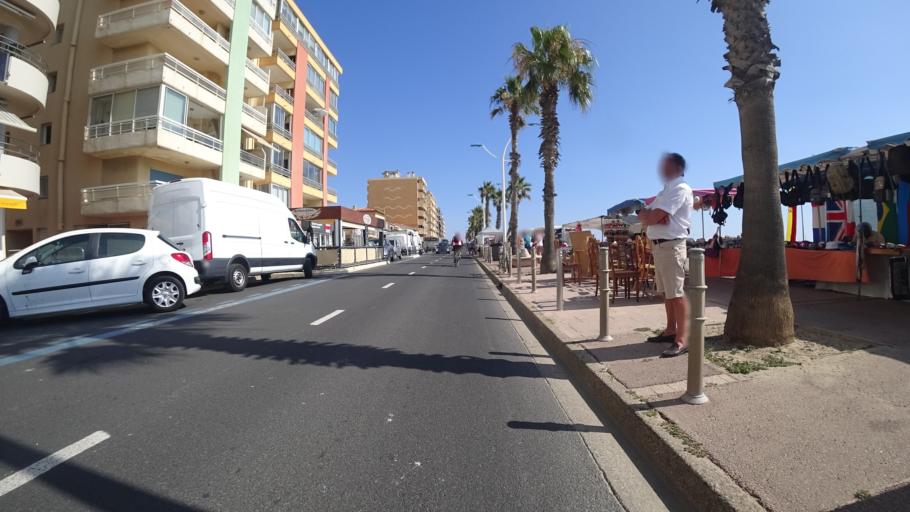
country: FR
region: Languedoc-Roussillon
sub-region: Departement des Pyrenees-Orientales
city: Canet-en-Roussillon
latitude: 42.6991
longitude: 3.0363
